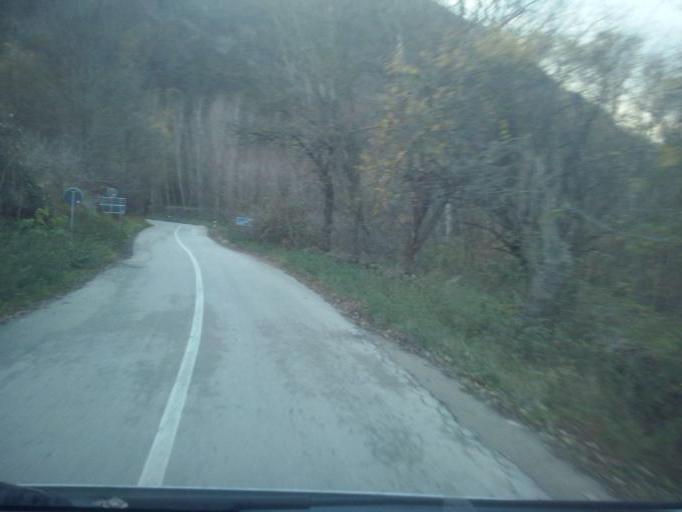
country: RS
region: Central Serbia
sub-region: Pirotski Okrug
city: Bela Palanka
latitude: 43.0321
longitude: 22.3989
